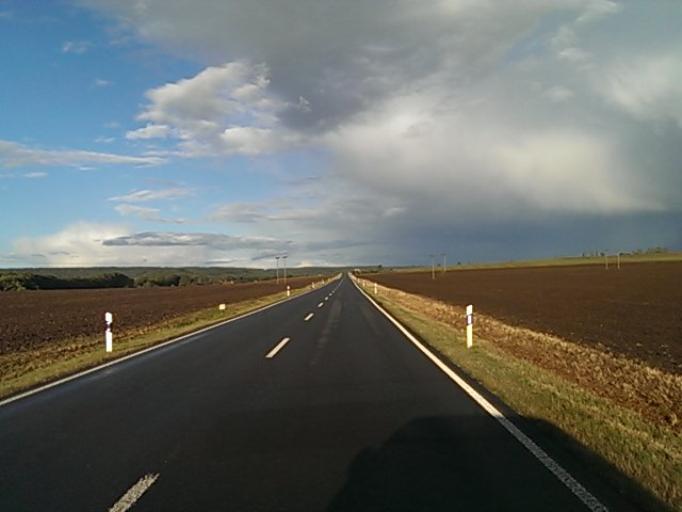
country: DE
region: Thuringia
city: Kolleda
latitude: 51.1937
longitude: 11.2663
